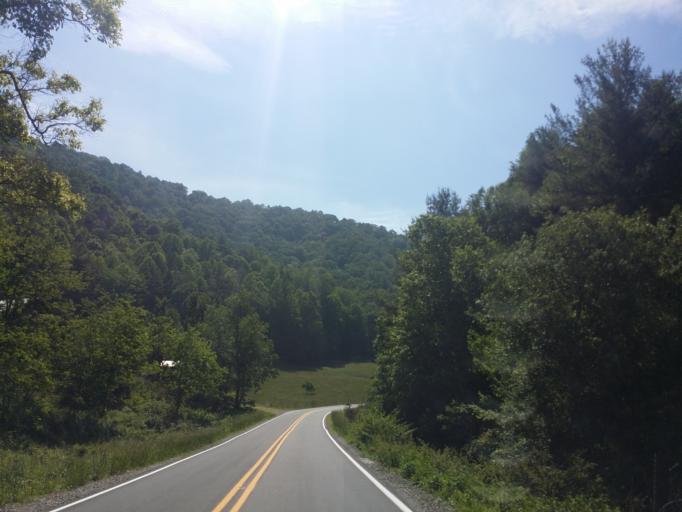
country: US
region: North Carolina
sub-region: Madison County
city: Marshall
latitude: 35.7457
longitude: -82.8587
